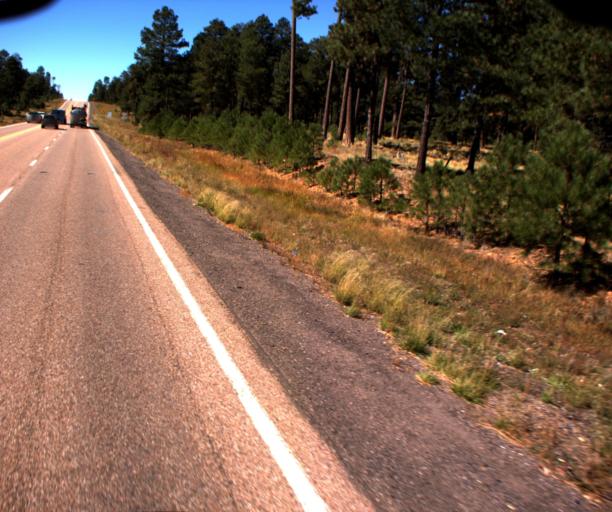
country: US
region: Arizona
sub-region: Navajo County
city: Heber-Overgaard
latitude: 34.3272
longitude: -110.8217
